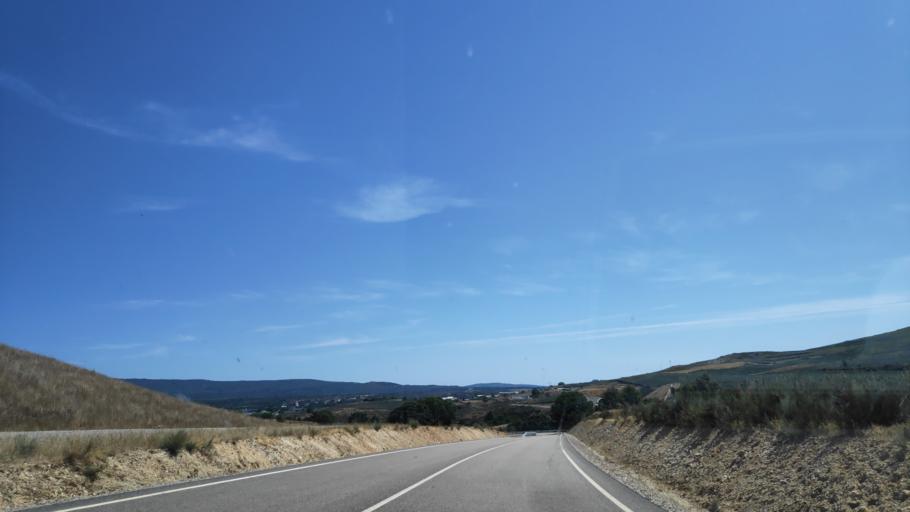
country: ES
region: Castille and Leon
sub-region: Provincia de Zamora
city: Puebla de Sanabria
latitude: 42.0464
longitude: -6.6506
